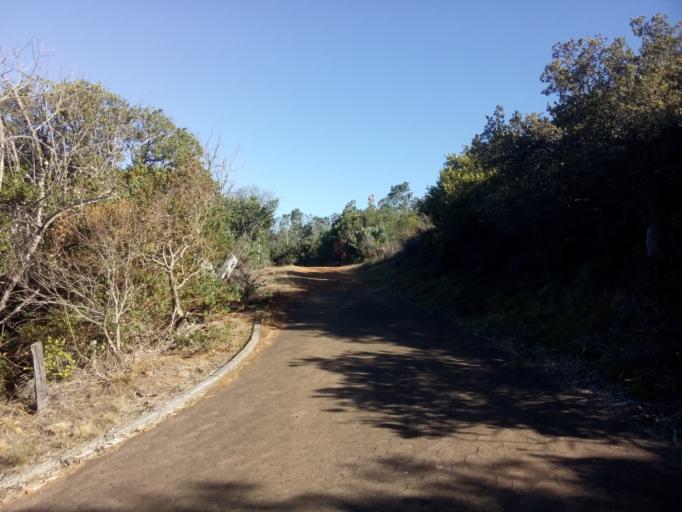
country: ZA
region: Western Cape
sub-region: City of Cape Town
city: Newlands
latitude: -33.9893
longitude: 18.4251
